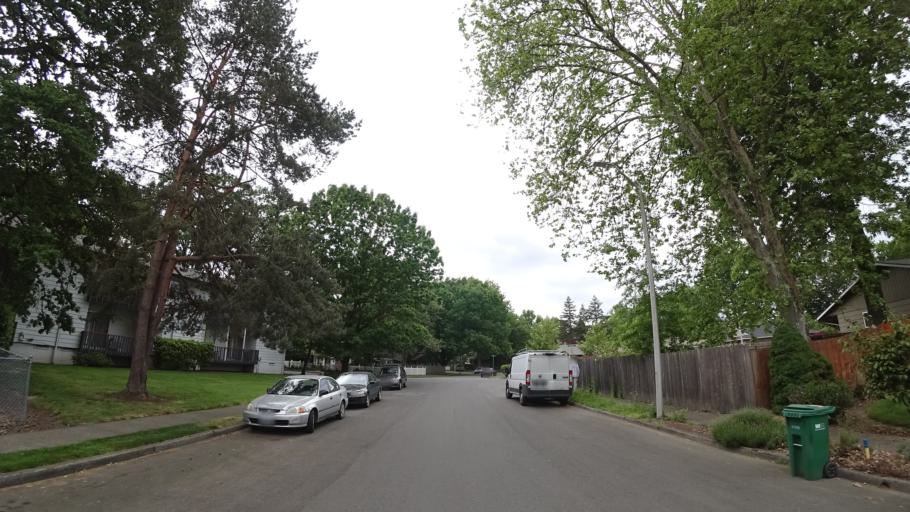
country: US
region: Oregon
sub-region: Washington County
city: Beaverton
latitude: 45.4843
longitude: -122.7898
